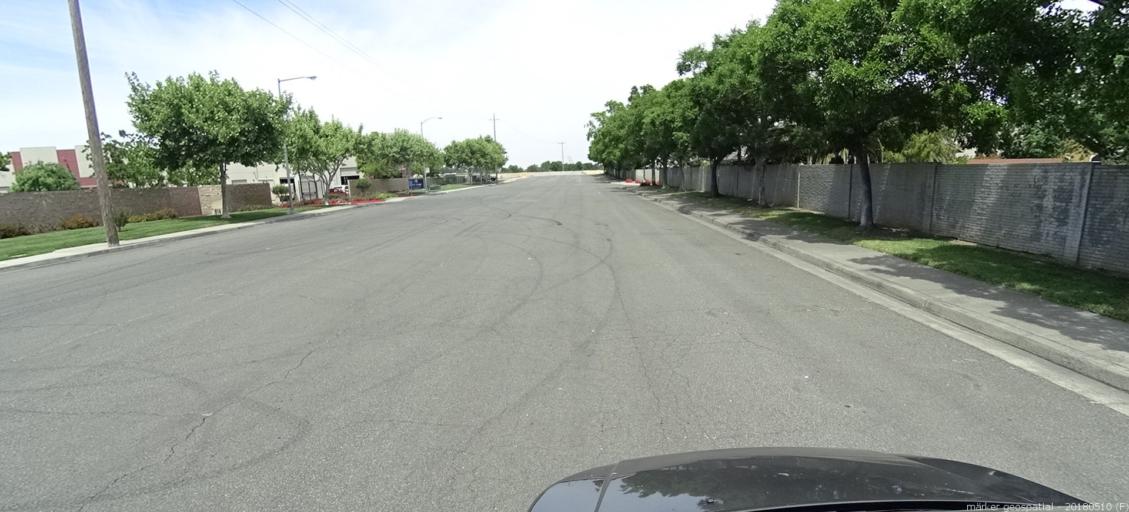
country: US
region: California
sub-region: Sacramento County
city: Rio Linda
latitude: 38.6572
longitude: -121.4661
